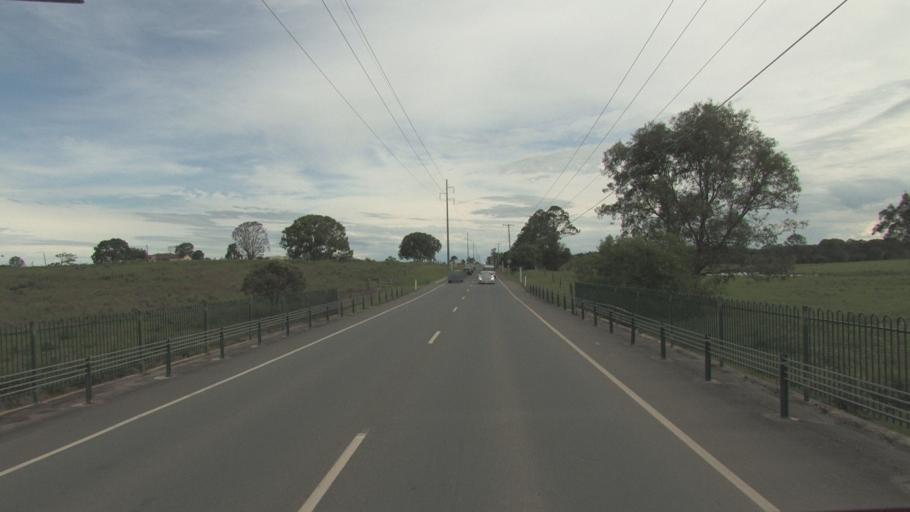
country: AU
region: Queensland
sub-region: Logan
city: Waterford West
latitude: -27.7014
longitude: 153.1178
